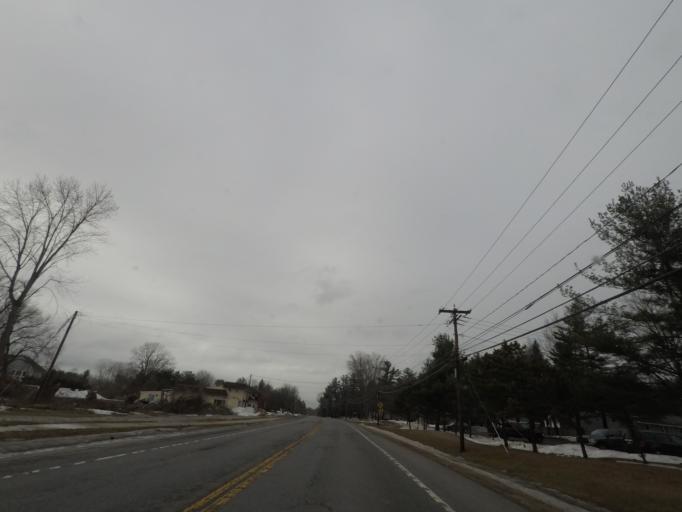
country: US
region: New York
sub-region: Albany County
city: Voorheesville
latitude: 42.7170
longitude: -73.9369
